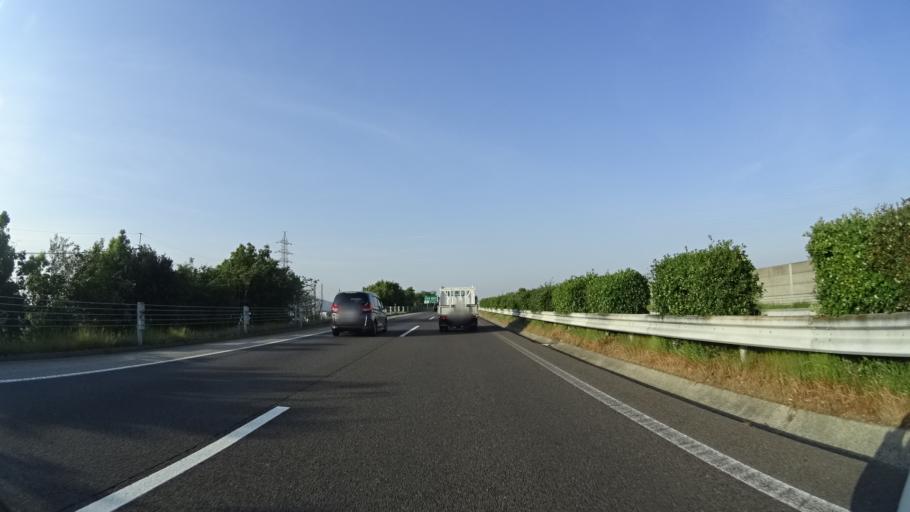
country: JP
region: Kagawa
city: Kan'onjicho
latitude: 34.0787
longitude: 133.6483
